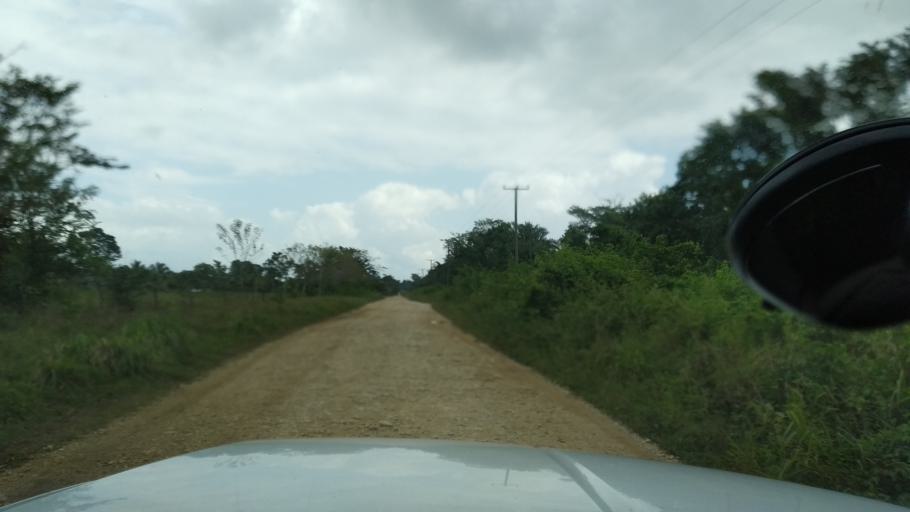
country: BZ
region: Toledo
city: Punta Gorda
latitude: 16.2175
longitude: -89.0033
